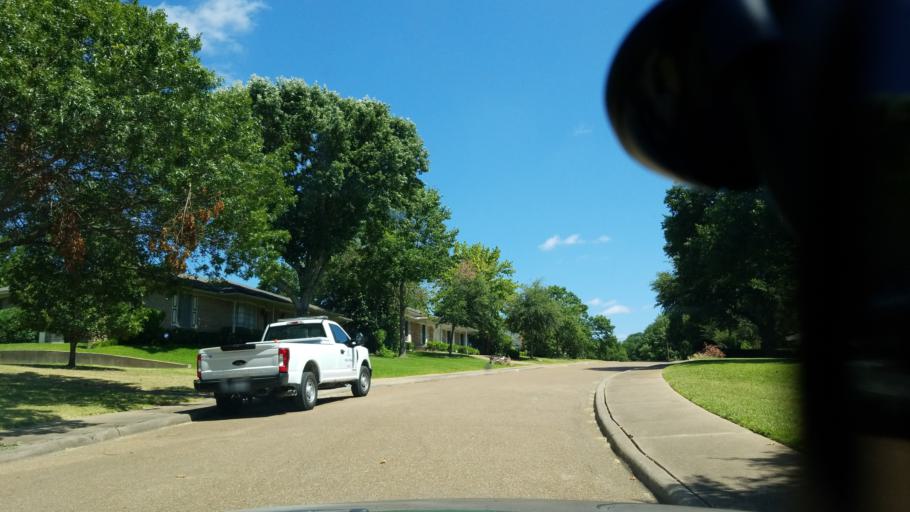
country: US
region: Texas
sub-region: Dallas County
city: Cockrell Hill
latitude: 32.6791
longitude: -96.8336
